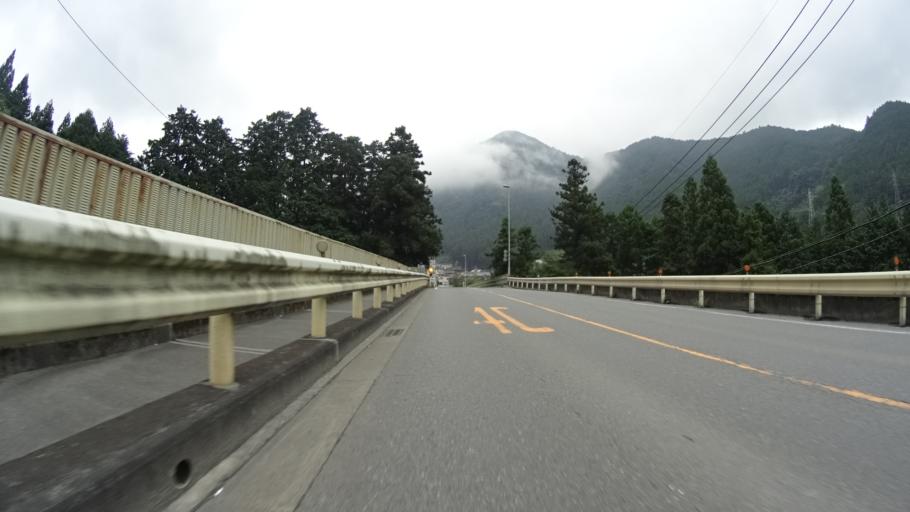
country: JP
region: Tokyo
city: Ome
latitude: 35.8134
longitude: 139.1531
